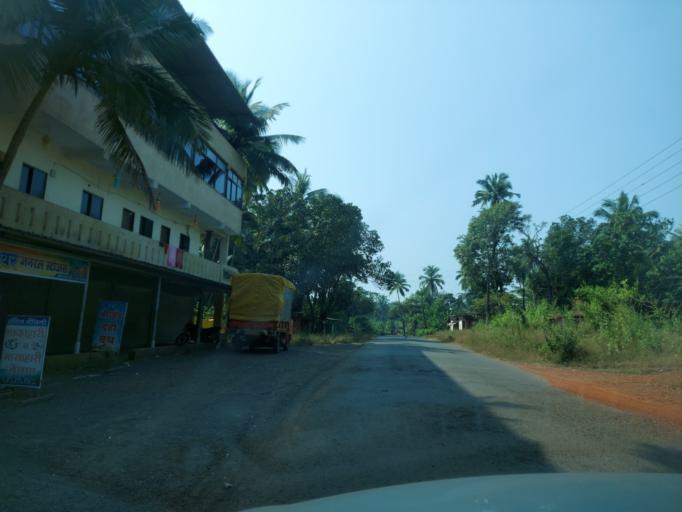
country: IN
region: Maharashtra
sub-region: Sindhudurg
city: Kudal
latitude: 15.9722
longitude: 73.6076
